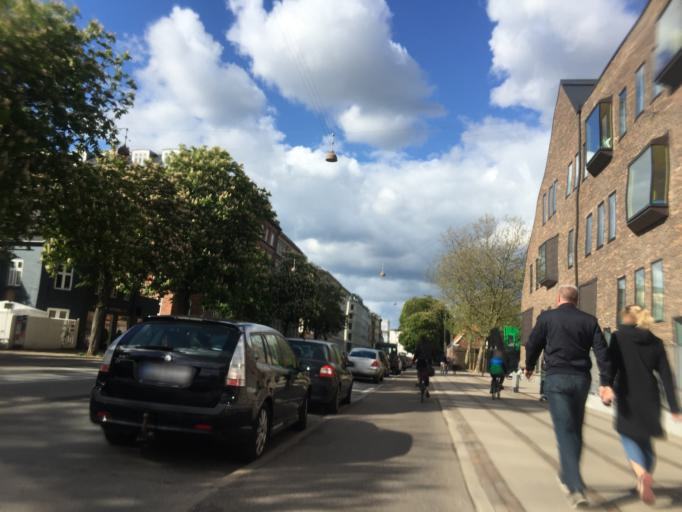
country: DK
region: Capital Region
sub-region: Kobenhavn
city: Copenhagen
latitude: 55.6930
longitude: 12.5778
